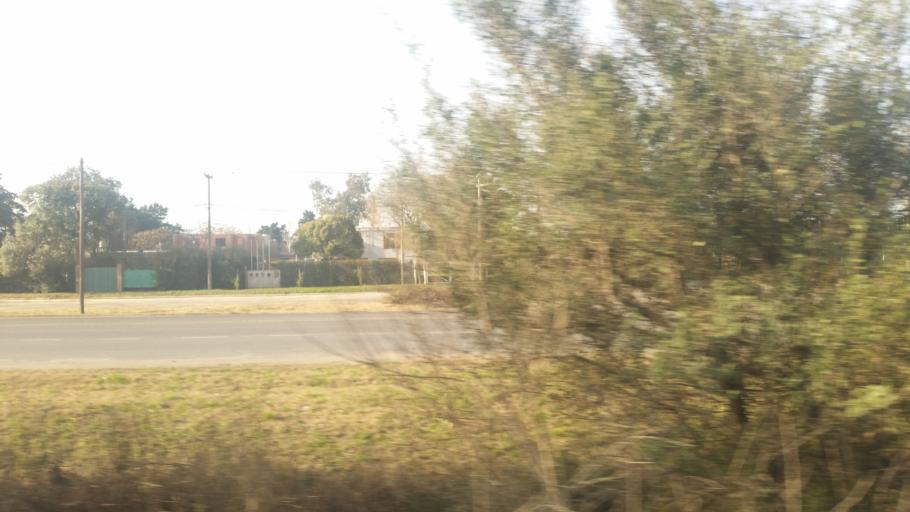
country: AR
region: Cordoba
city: Toledo
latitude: -31.5648
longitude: -64.0006
